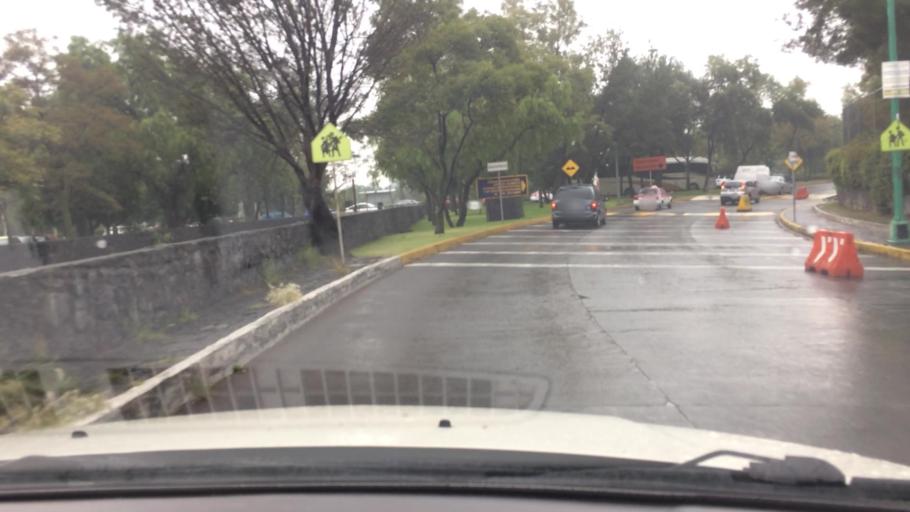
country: MX
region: Mexico City
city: Magdalena Contreras
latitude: 19.3358
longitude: -99.1931
